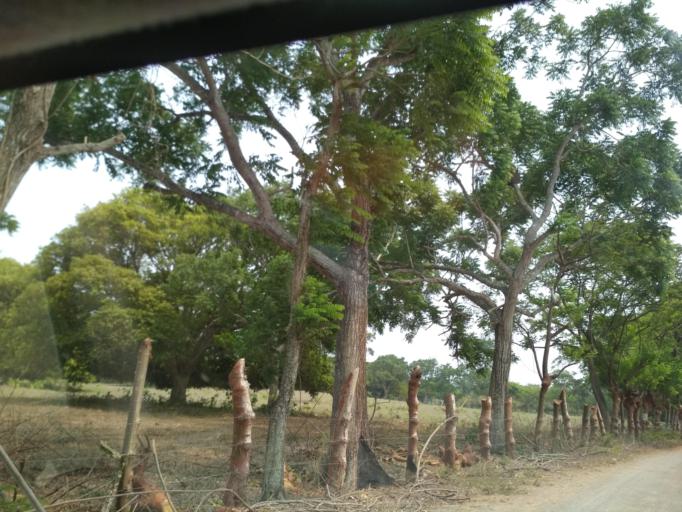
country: MX
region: Veracruz
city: El Tejar
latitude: 19.0660
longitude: -96.1537
